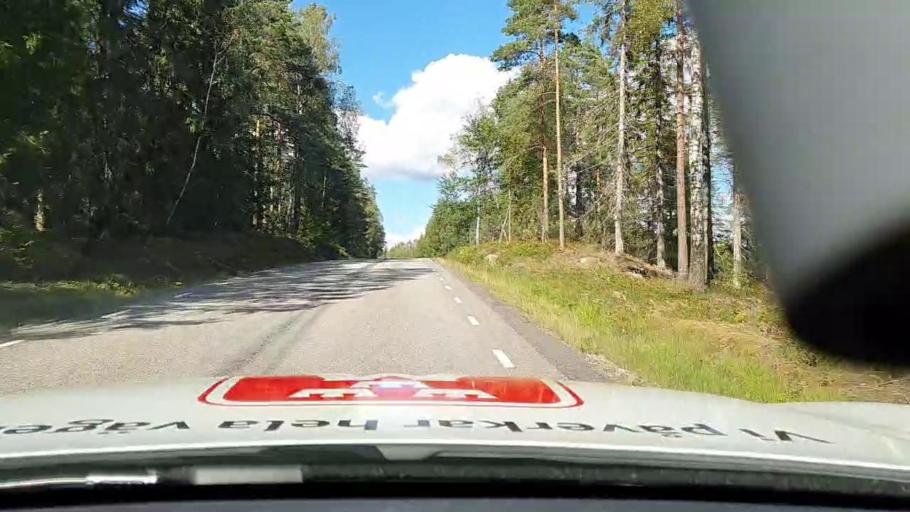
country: SE
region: Vaestra Goetaland
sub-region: Marks Kommun
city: Fritsla
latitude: 57.3786
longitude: 12.8589
